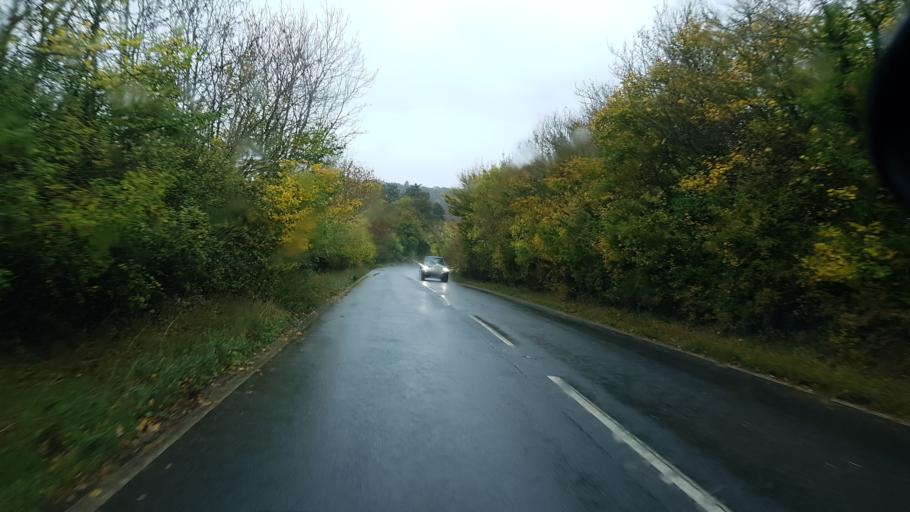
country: GB
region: England
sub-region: Gloucestershire
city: Stow on the Wold
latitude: 51.9127
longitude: -1.7225
